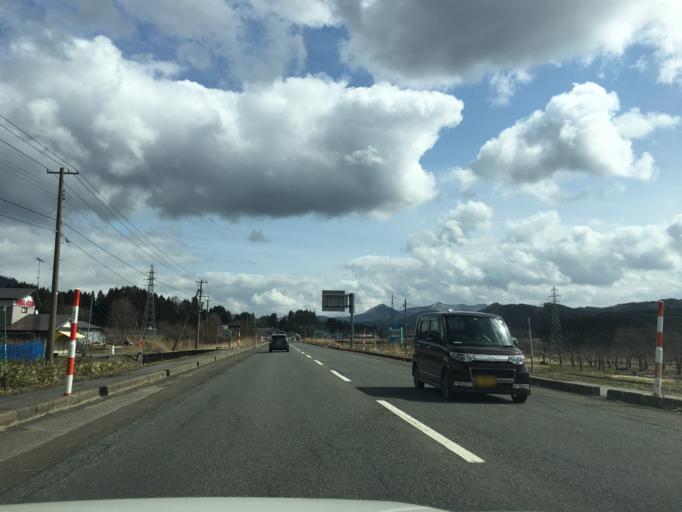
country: JP
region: Akita
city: Odate
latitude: 40.2295
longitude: 140.5949
